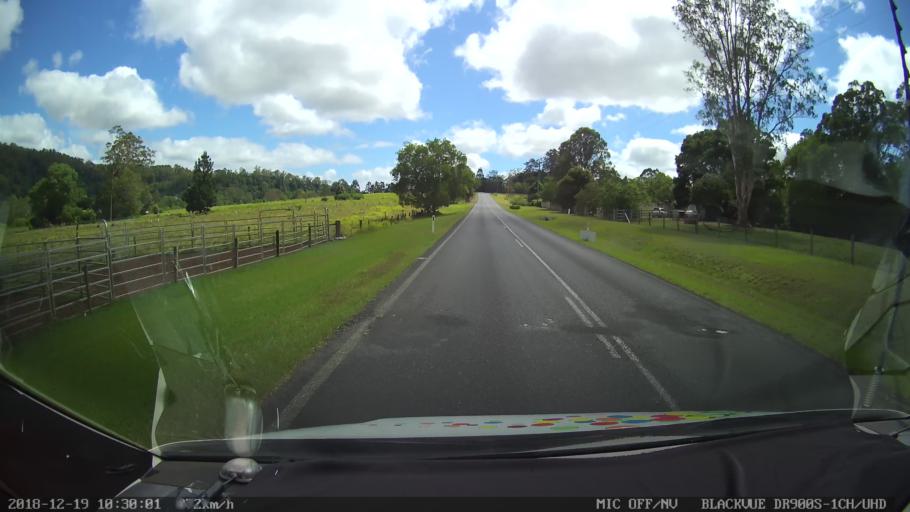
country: AU
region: New South Wales
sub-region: Lismore Municipality
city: Larnook
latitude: -28.5915
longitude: 153.1035
